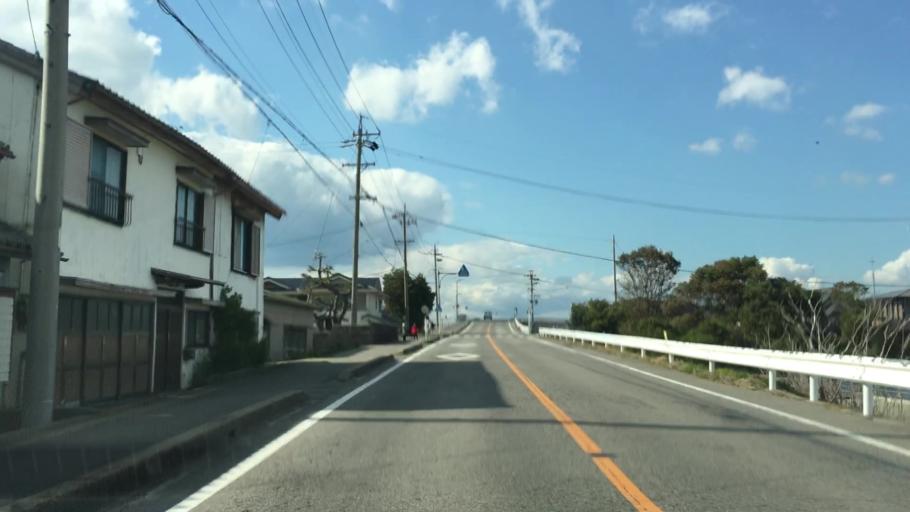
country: JP
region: Aichi
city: Ishiki
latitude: 34.7870
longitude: 137.0279
